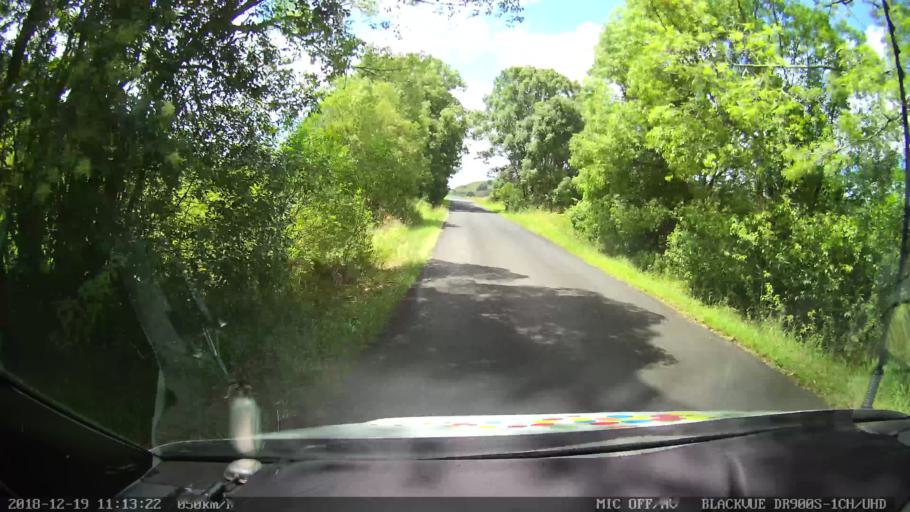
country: AU
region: New South Wales
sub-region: Lismore Municipality
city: Nimbin
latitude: -28.6552
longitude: 153.2636
